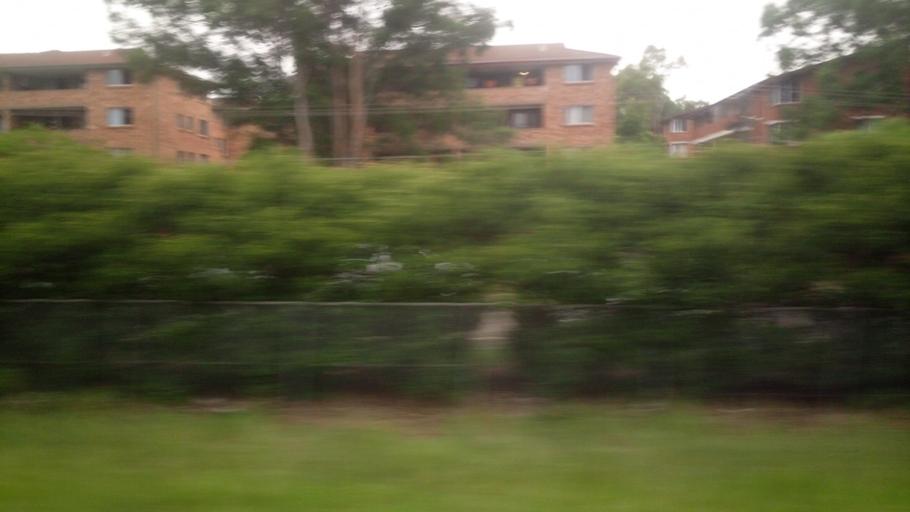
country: AU
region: New South Wales
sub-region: Penrith Municipality
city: Cambridge Park
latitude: -33.7591
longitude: 150.7239
